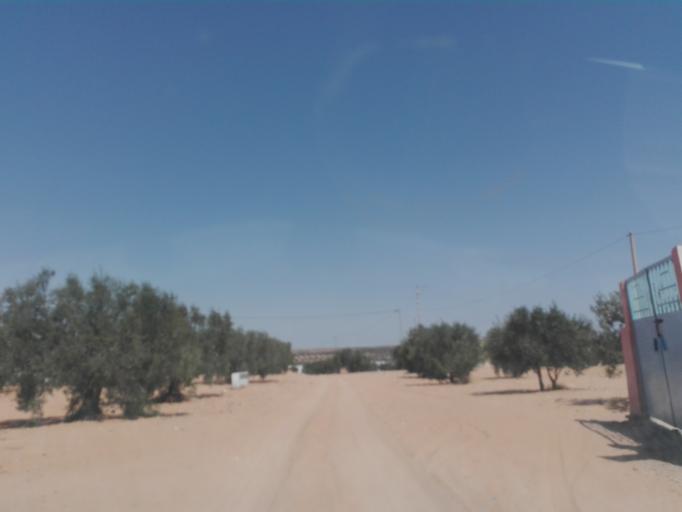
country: TN
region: Safaqis
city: Bi'r `Ali Bin Khalifah
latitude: 34.6480
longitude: 10.2539
